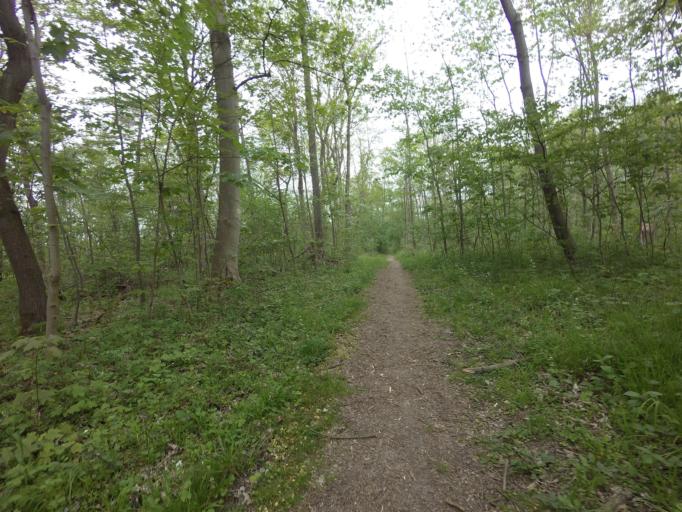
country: DE
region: Lower Saxony
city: Diekholzen
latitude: 52.1392
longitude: 9.9044
